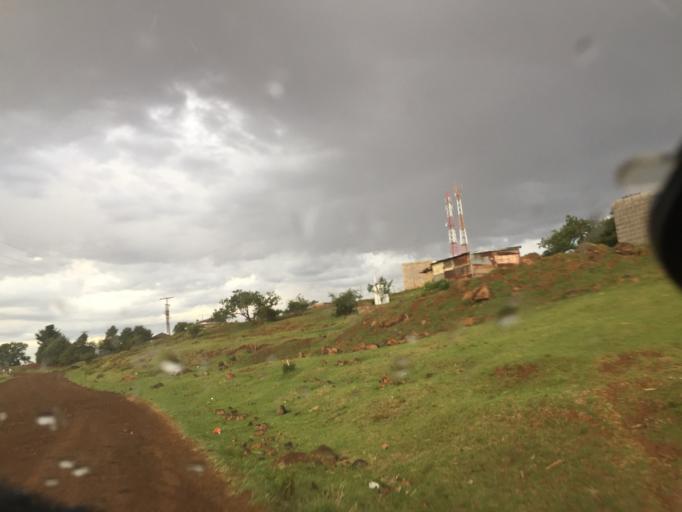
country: LS
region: Berea
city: Teyateyaneng
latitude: -29.1580
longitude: 28.0342
